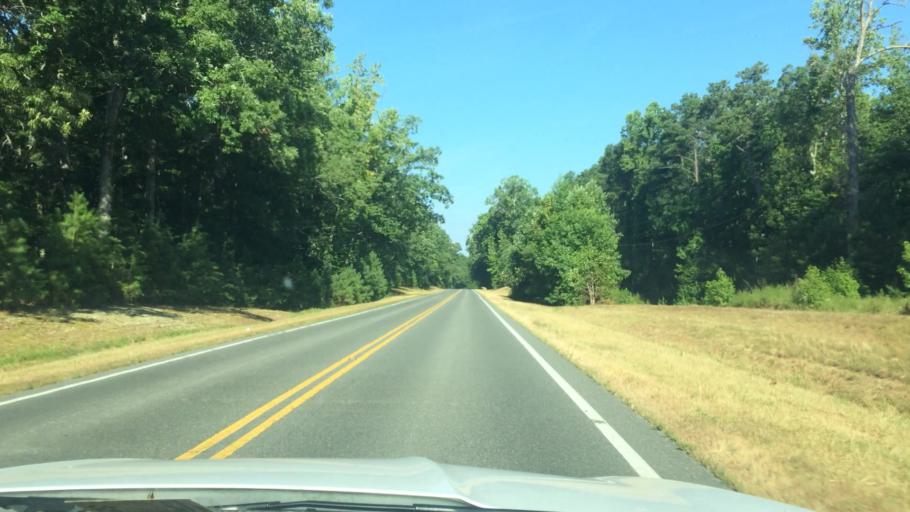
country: US
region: Virginia
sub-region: Lancaster County
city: Lancaster
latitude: 37.8272
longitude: -76.5665
